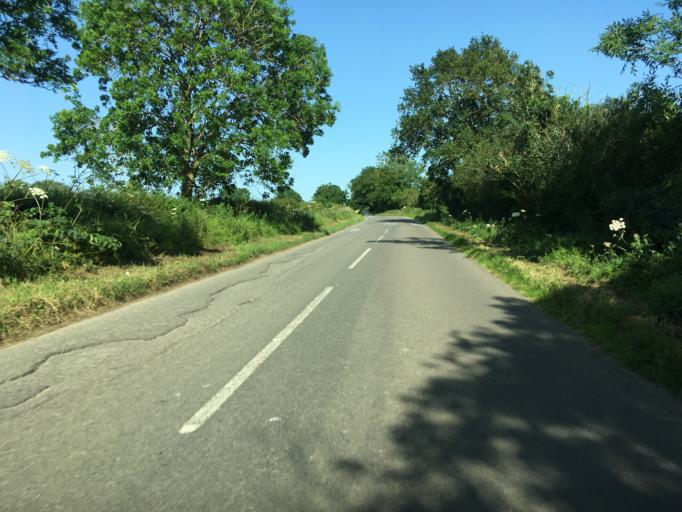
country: GB
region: England
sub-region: Buckinghamshire
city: Steeple Claydon
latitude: 51.9334
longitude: -1.0157
